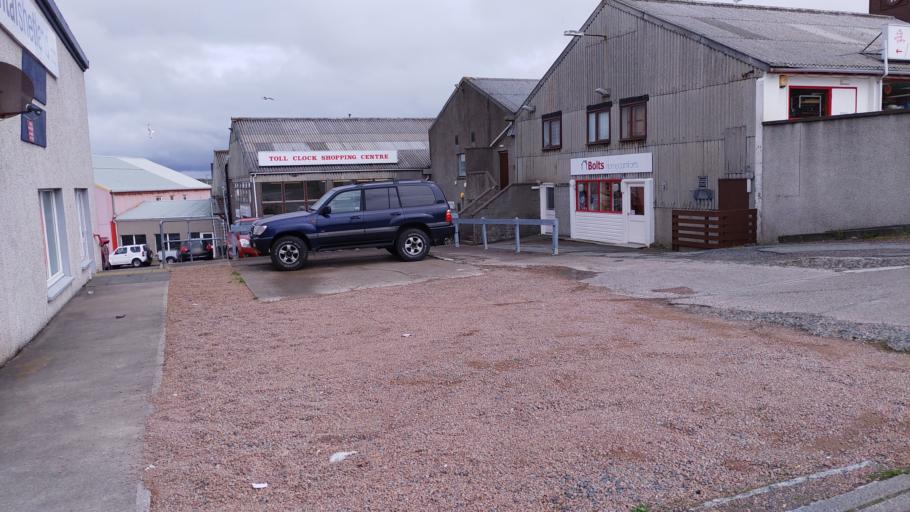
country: GB
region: Scotland
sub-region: Shetland Islands
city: Lerwick
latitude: 60.1576
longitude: -1.1555
